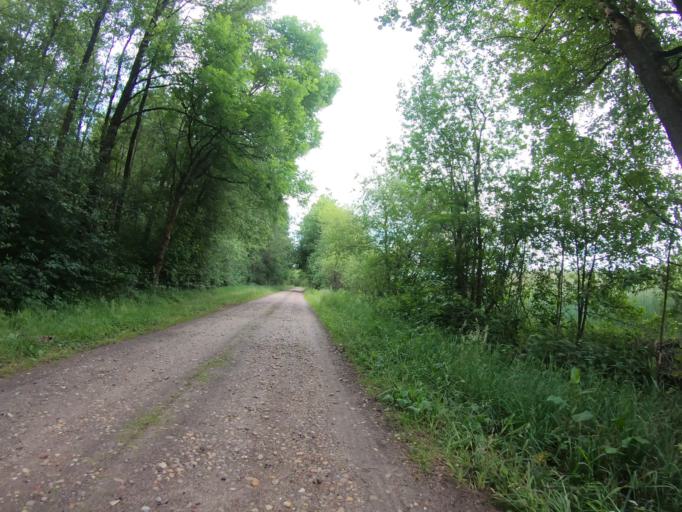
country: DE
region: Lower Saxony
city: Wesendorf
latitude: 52.5699
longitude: 10.5629
